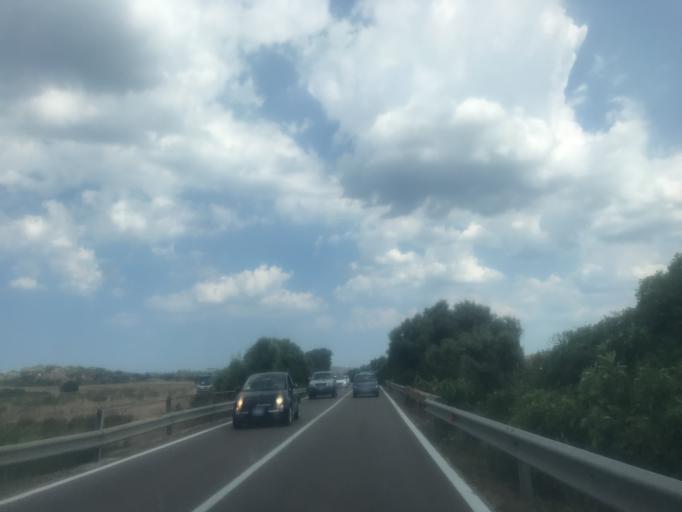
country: IT
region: Sardinia
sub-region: Provincia di Olbia-Tempio
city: San Teodoro
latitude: 40.8724
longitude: 9.6319
